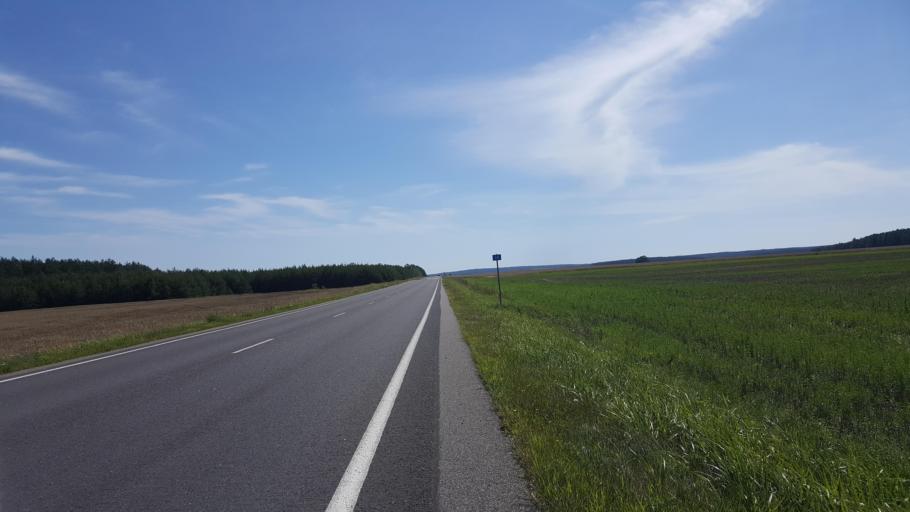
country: BY
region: Brest
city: Kamyanyets
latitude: 52.3929
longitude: 23.9445
